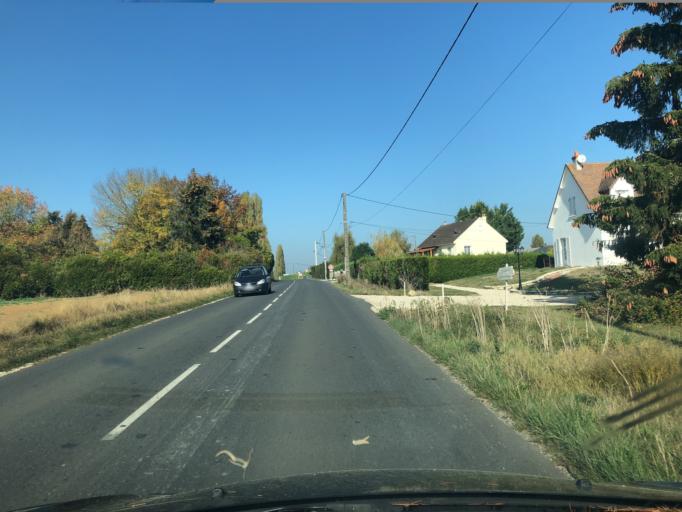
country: FR
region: Centre
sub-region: Departement d'Indre-et-Loire
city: Mettray
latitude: 47.4496
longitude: 0.6754
